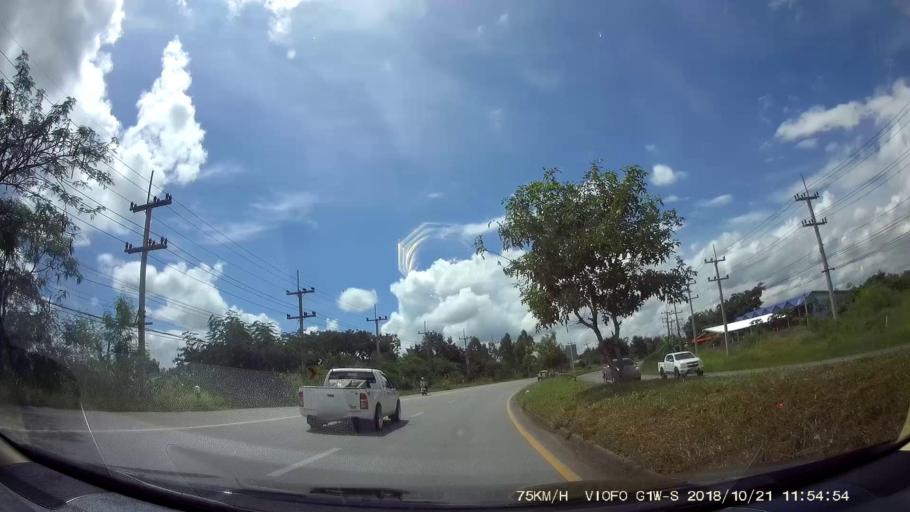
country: TH
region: Chaiyaphum
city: Chatturat
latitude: 15.5799
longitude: 101.8980
